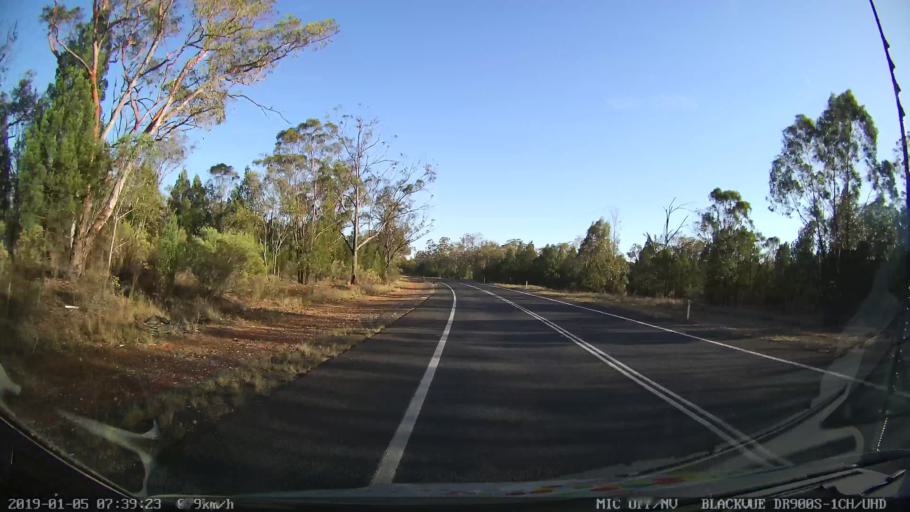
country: AU
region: New South Wales
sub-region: Gilgandra
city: Gilgandra
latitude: -31.9382
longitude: 148.6197
